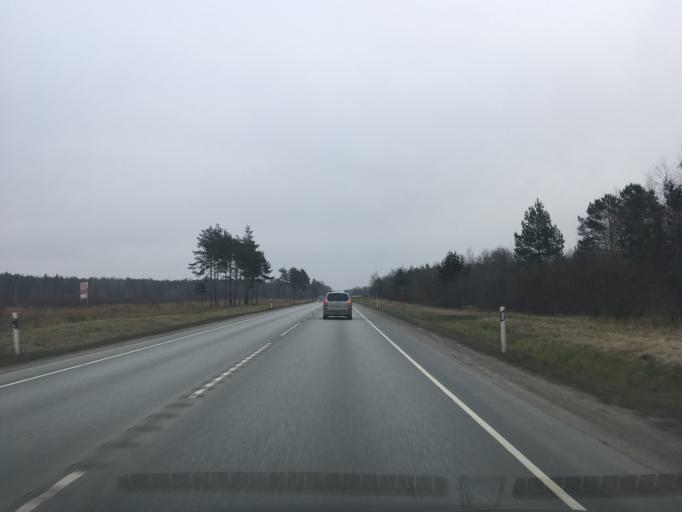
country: EE
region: Ida-Virumaa
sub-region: Johvi vald
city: Johvi
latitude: 59.3671
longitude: 27.4268
